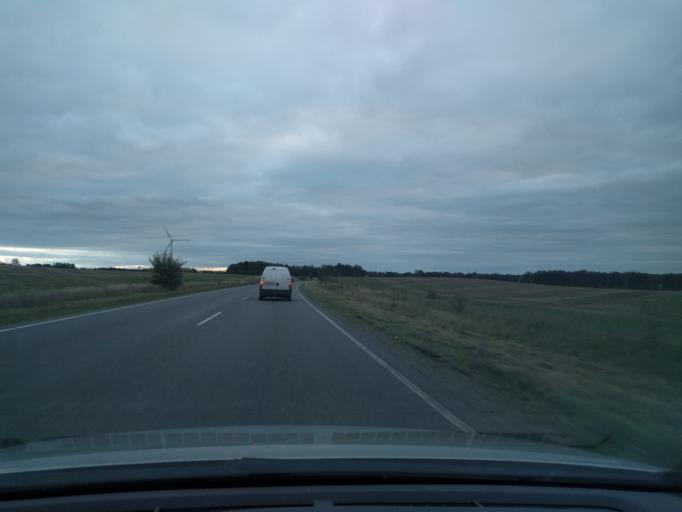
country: DK
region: South Denmark
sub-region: Faaborg-Midtfyn Kommune
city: Arslev
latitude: 55.2917
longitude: 10.4079
